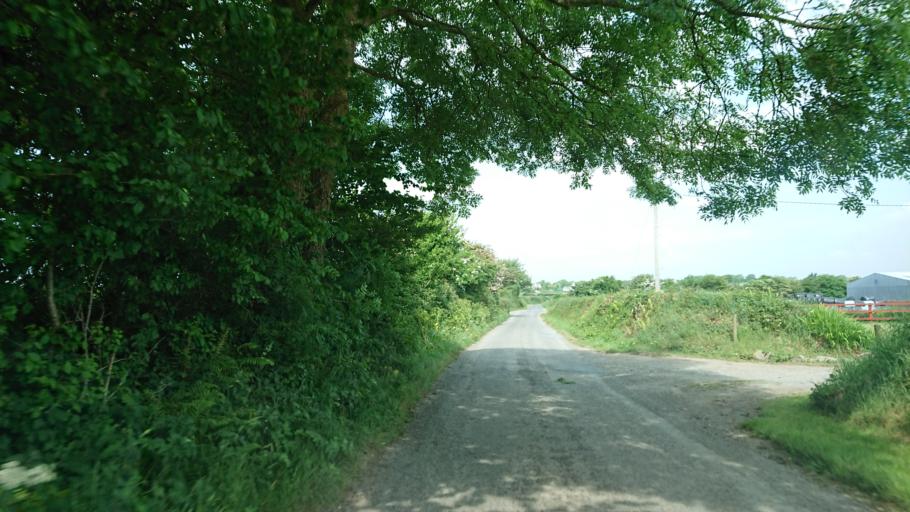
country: IE
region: Munster
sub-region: Waterford
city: Dunmore East
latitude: 52.2118
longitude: -6.9949
